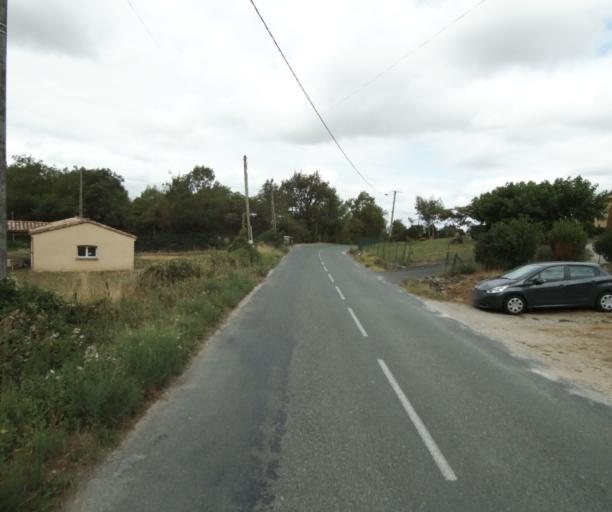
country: FR
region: Midi-Pyrenees
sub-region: Departement du Tarn
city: Soreze
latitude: 43.4503
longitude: 2.0731
